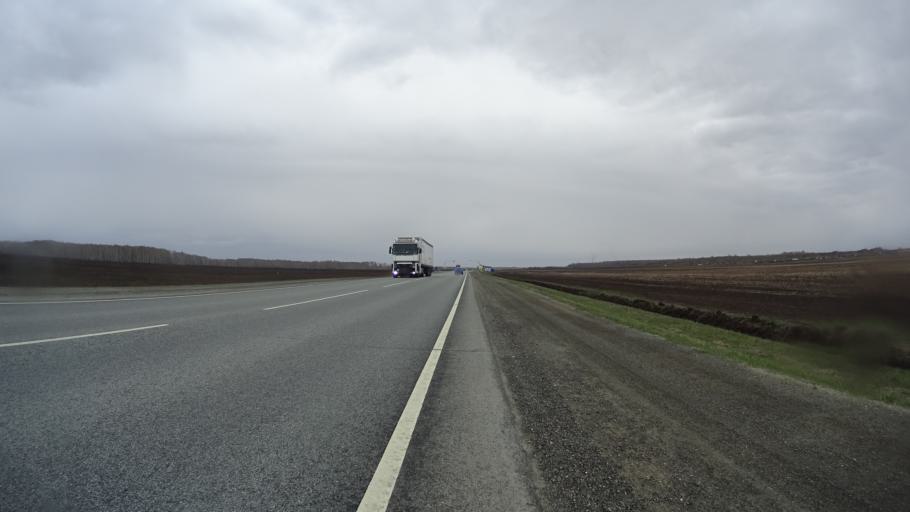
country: RU
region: Chelyabinsk
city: Krasnogorskiy
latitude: 54.5842
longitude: 61.2909
